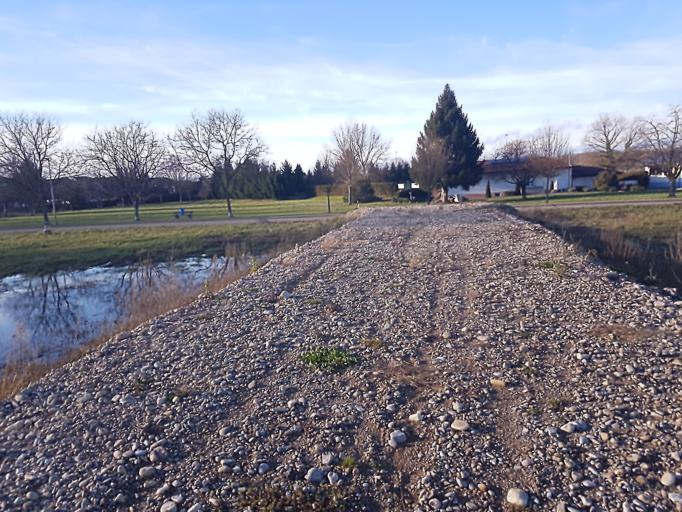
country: DE
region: Baden-Wuerttemberg
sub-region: Freiburg Region
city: Schallstadt
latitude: 47.9601
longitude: 7.7566
